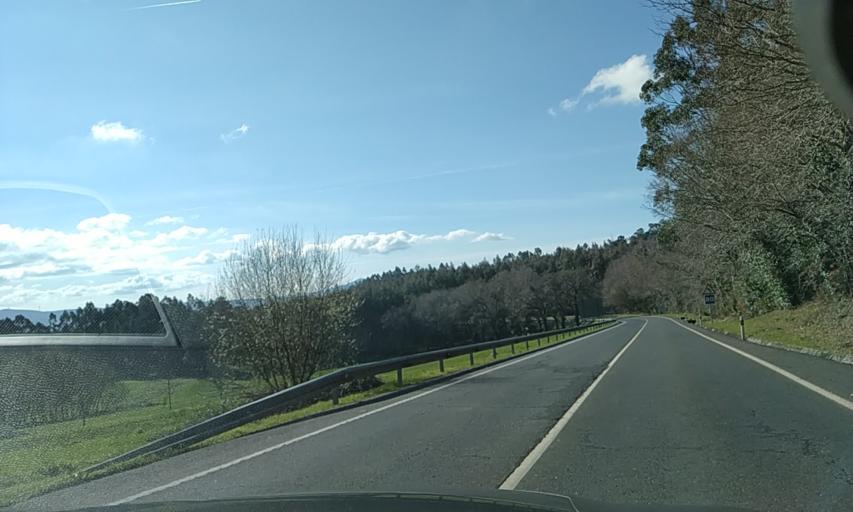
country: ES
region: Galicia
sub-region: Provincia da Coruna
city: Ribeira
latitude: 42.7073
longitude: -8.4177
